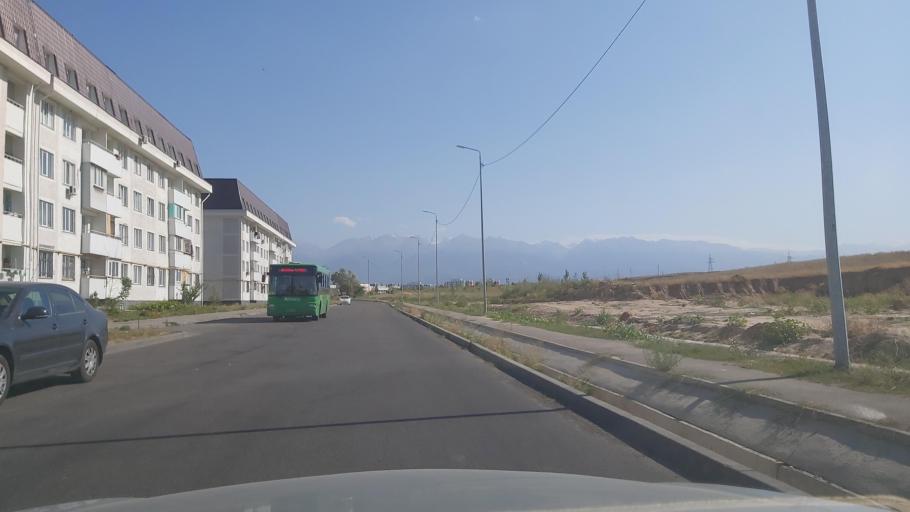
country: KZ
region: Almaty Oblysy
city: Burunday
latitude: 43.3196
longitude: 76.8391
